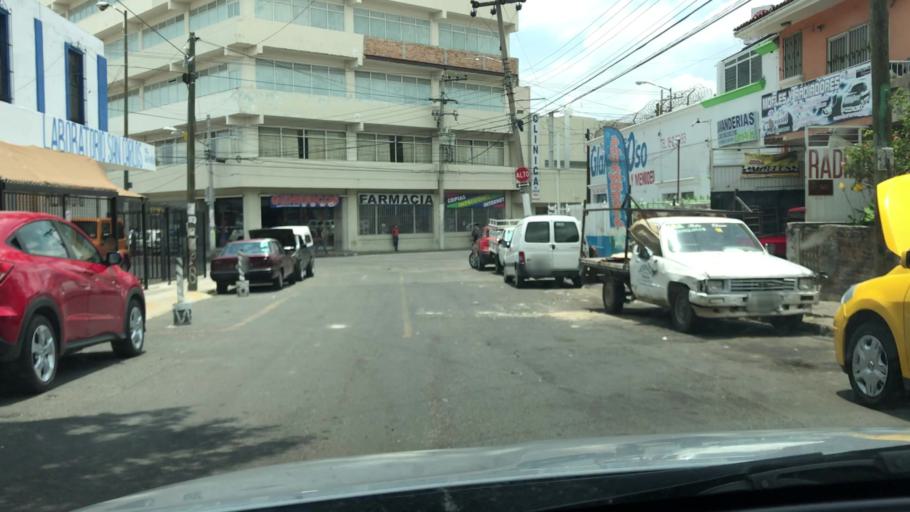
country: MX
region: Jalisco
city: Zapopan2
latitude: 20.7307
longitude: -103.4040
